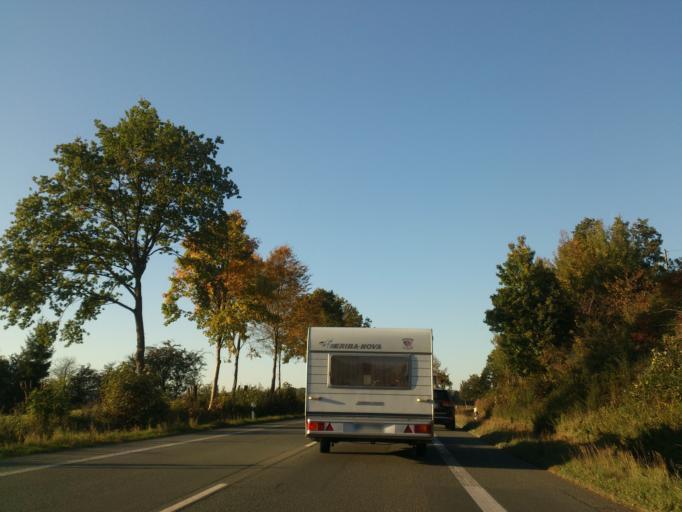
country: DE
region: North Rhine-Westphalia
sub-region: Regierungsbezirk Detmold
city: Willebadessen
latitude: 51.6484
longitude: 9.0114
